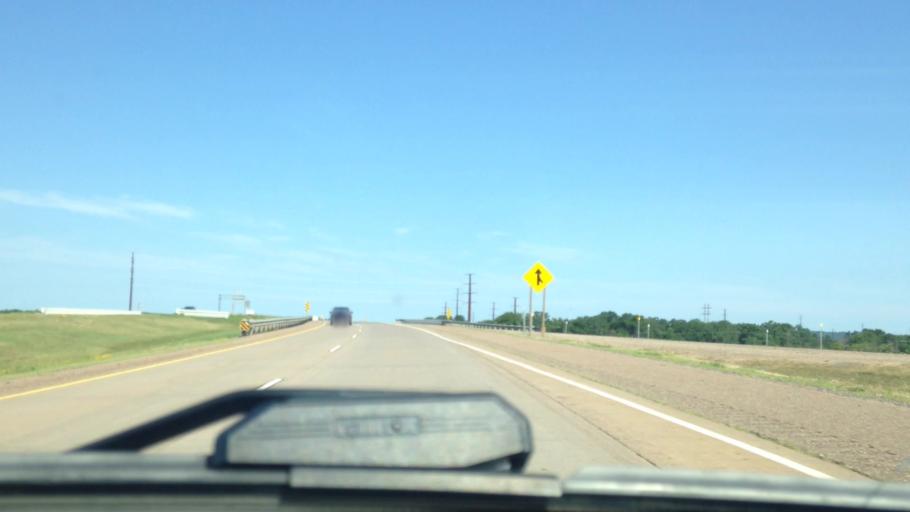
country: US
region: Wisconsin
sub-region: Chippewa County
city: Lake Hallie
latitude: 44.8931
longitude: -91.4158
